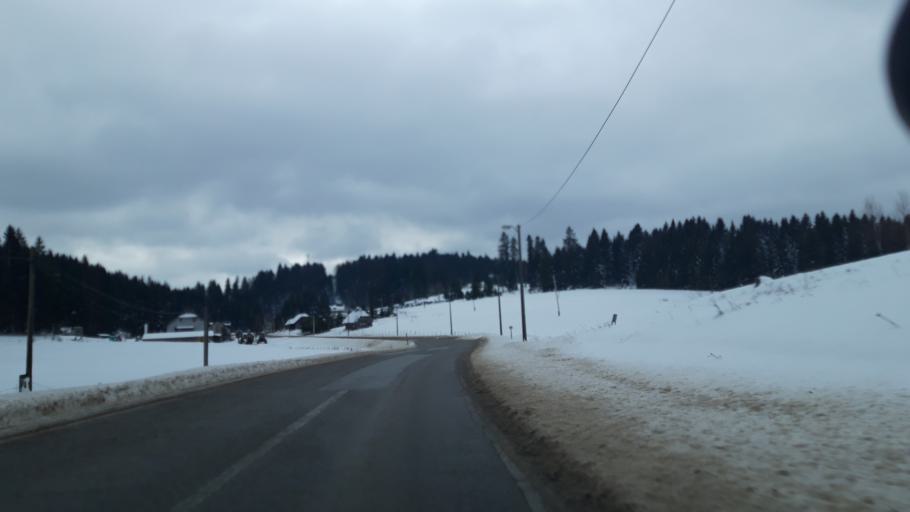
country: BA
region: Republika Srpska
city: Han Pijesak
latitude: 44.0935
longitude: 18.9560
